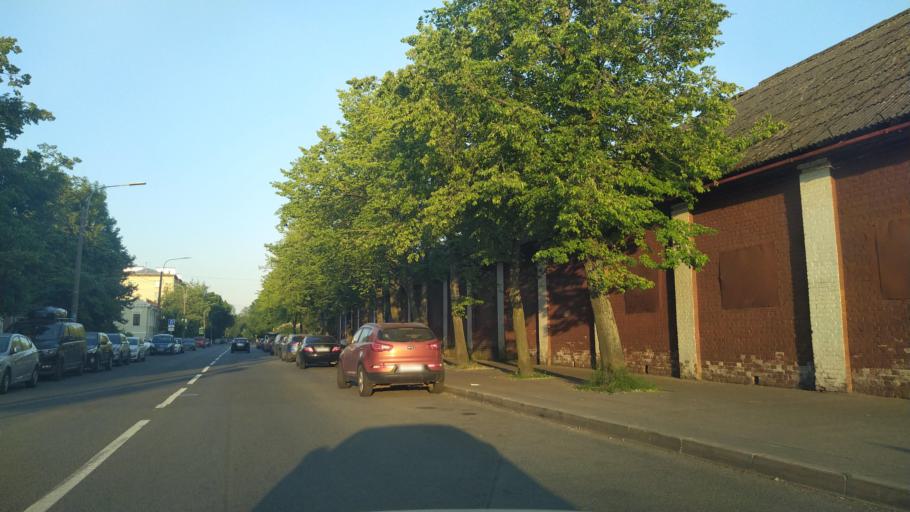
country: RU
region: St.-Petersburg
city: Kronshtadt
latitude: 59.9918
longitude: 29.7548
